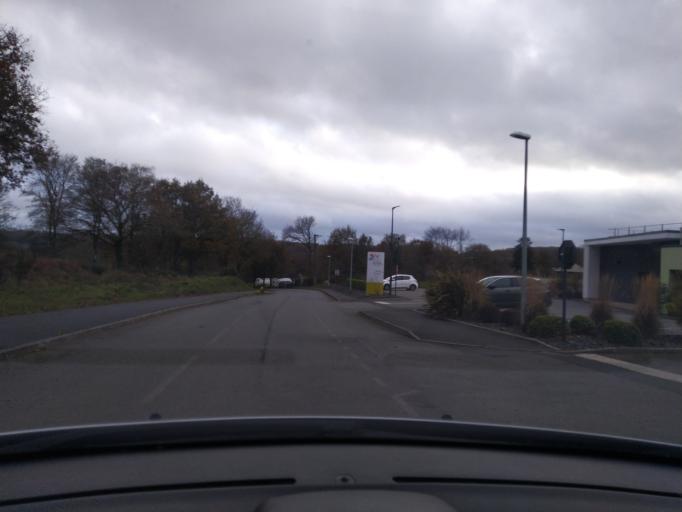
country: FR
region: Brittany
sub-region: Departement du Finistere
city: Guerlesquin
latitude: 48.5138
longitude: -3.5897
